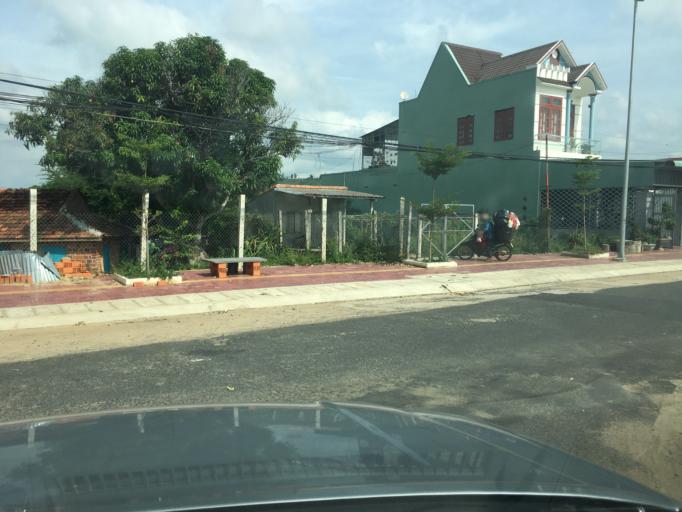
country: VN
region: Gia Lai
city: Kong Chro
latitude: 13.7727
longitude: 108.5224
